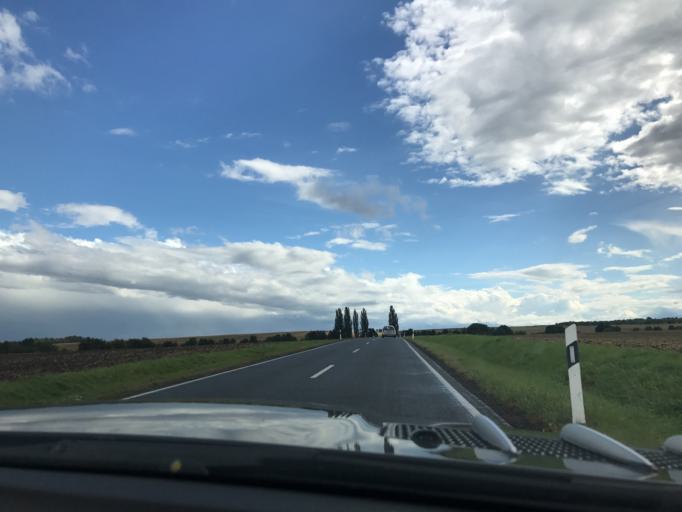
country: DE
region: Thuringia
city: Heroldishausen
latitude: 51.1100
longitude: 10.5333
